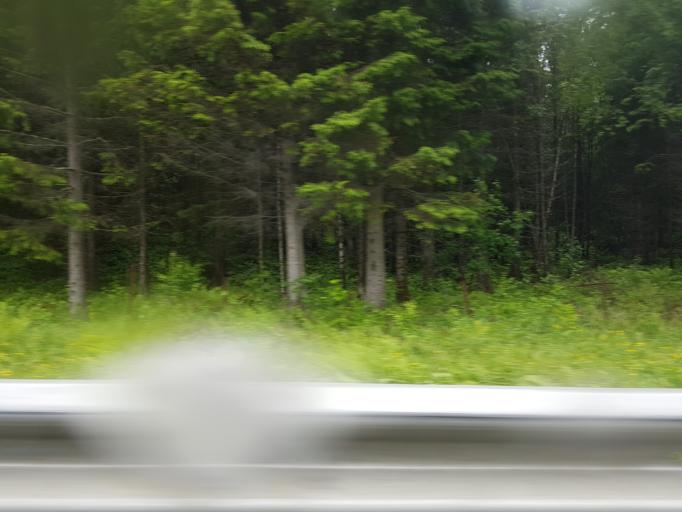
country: NO
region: Nord-Trondelag
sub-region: Stjordal
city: Stjordalshalsen
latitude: 63.4009
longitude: 10.9468
